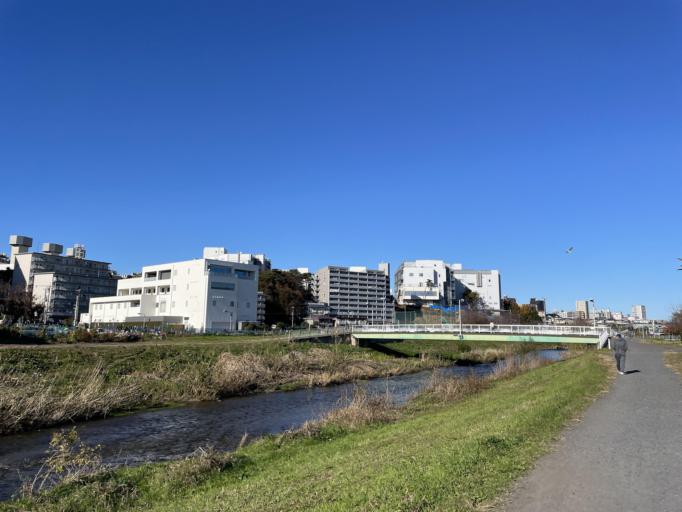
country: JP
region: Saitama
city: Asaka
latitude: 35.8056
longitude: 139.5841
